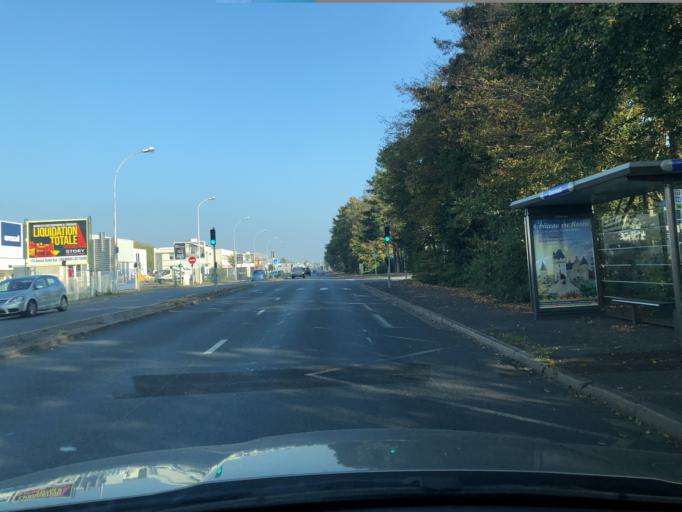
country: FR
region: Centre
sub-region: Departement d'Indre-et-Loire
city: Chanceaux-sur-Choisille
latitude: 47.4326
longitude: 0.6978
